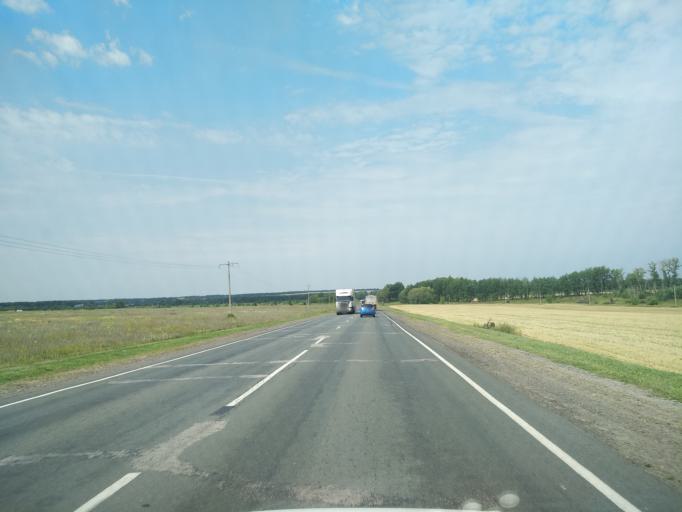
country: RU
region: Voronezj
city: Orlovo
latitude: 51.6799
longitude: 39.6203
